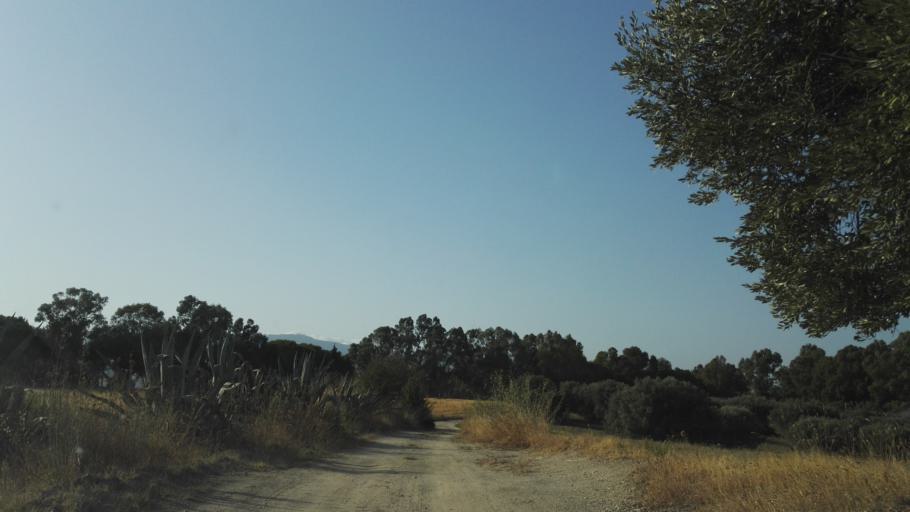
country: IT
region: Calabria
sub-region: Provincia di Reggio Calabria
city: Riace Marina
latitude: 38.3731
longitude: 16.4960
